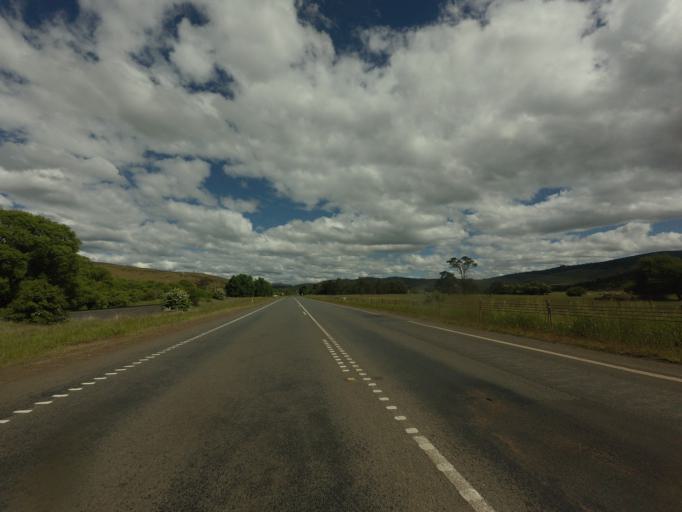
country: AU
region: Tasmania
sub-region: Brighton
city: Bridgewater
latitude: -42.1831
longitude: 147.3864
